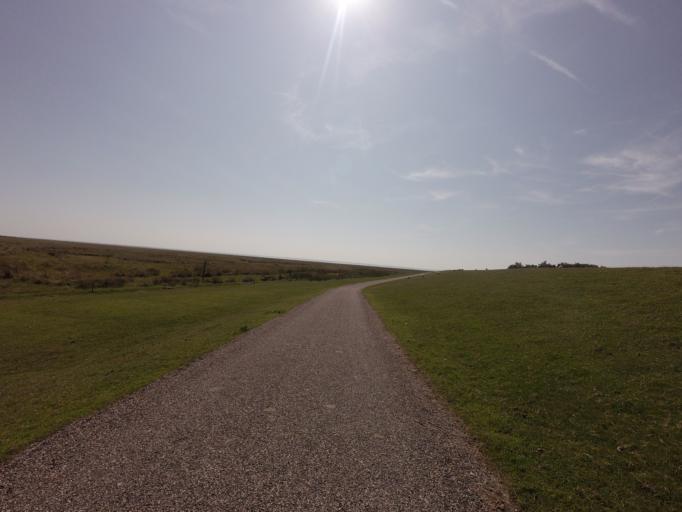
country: NL
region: Friesland
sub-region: Gemeente Schiermonnikoog
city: Schiermonnikoog
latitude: 53.4798
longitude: 6.2105
